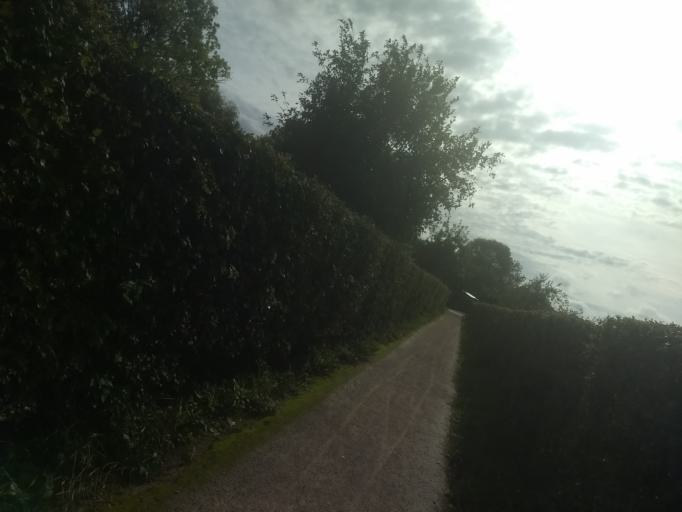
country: FR
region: Nord-Pas-de-Calais
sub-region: Departement du Pas-de-Calais
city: Achicourt
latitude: 50.2771
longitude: 2.7588
